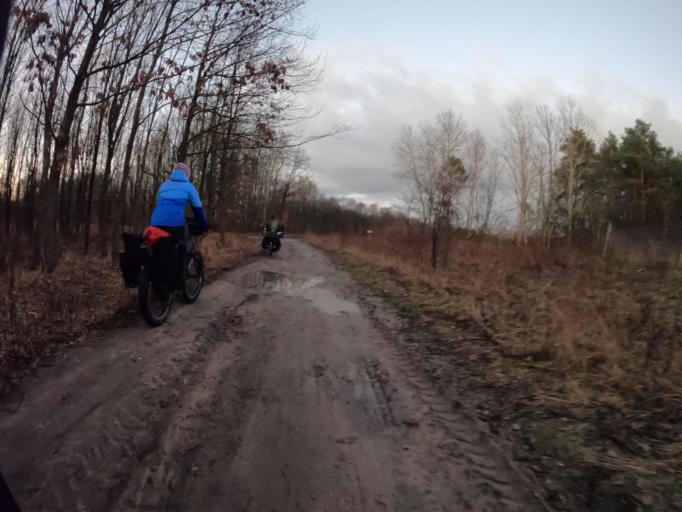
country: PL
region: Greater Poland Voivodeship
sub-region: Powiat zlotowski
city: Sypniewo
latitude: 53.4840
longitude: 16.6408
